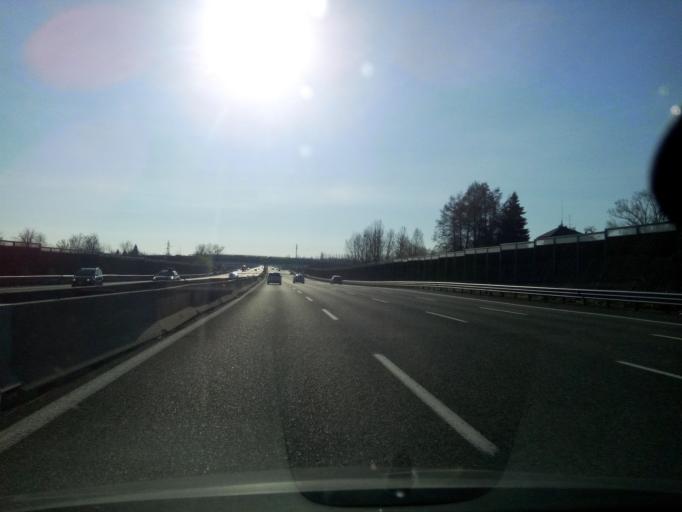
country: IT
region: Emilia-Romagna
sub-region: Provincia di Modena
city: San Damaso
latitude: 44.5808
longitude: 10.9737
